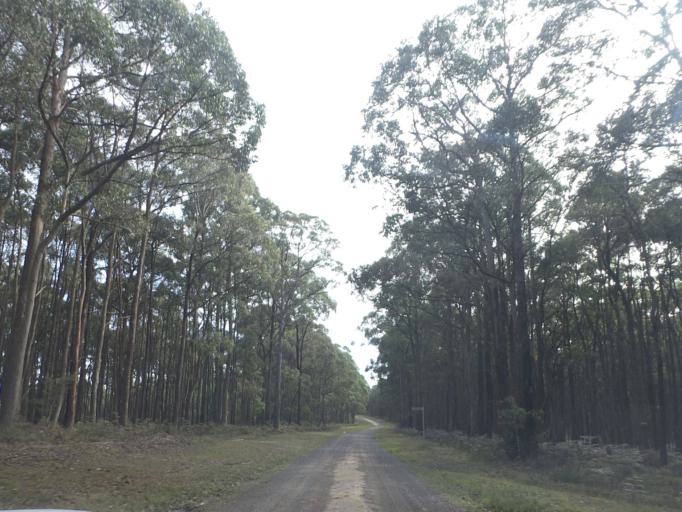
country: AU
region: Victoria
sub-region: Moorabool
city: Bacchus Marsh
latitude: -37.4745
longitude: 144.2133
